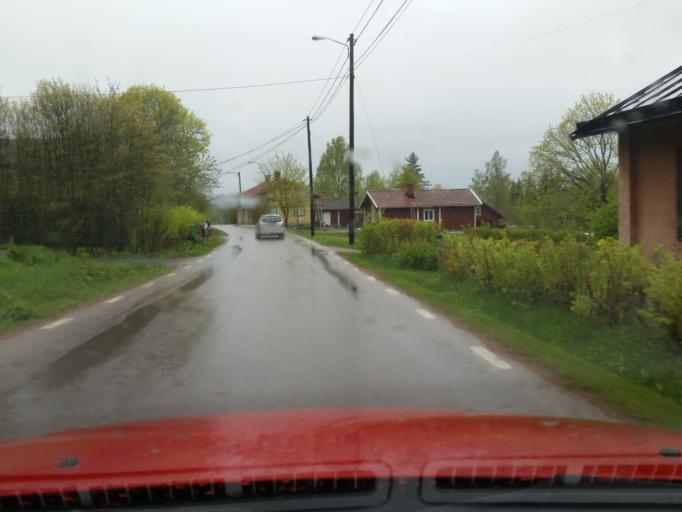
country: SE
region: Dalarna
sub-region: Saters Kommun
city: Saeter
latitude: 60.3596
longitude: 15.7877
